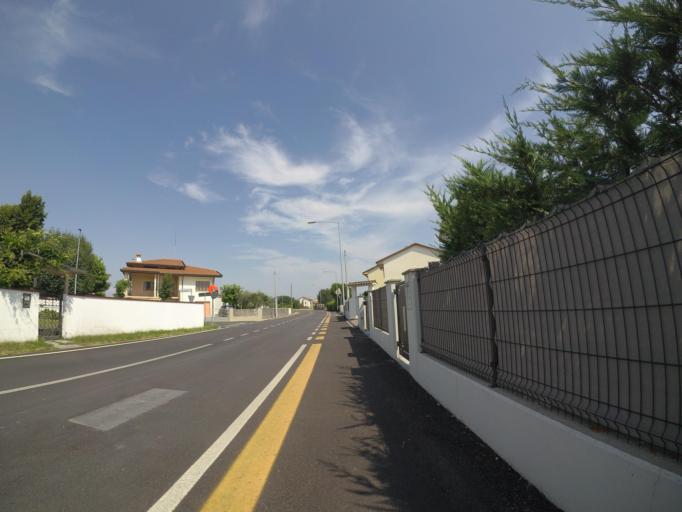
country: IT
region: Friuli Venezia Giulia
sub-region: Provincia di Pordenone
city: Rosa
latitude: 45.9195
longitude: 12.8760
